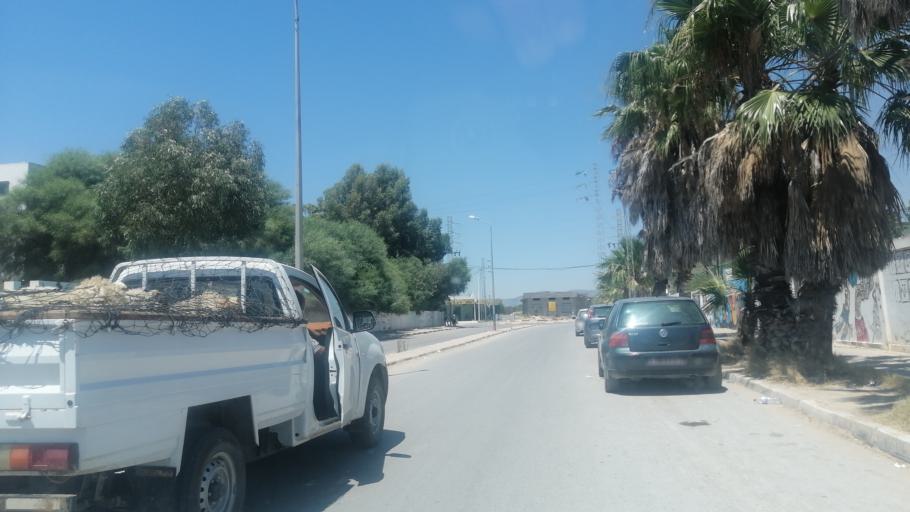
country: TN
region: Al Qayrawan
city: Sbikha
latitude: 36.1209
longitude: 10.0897
